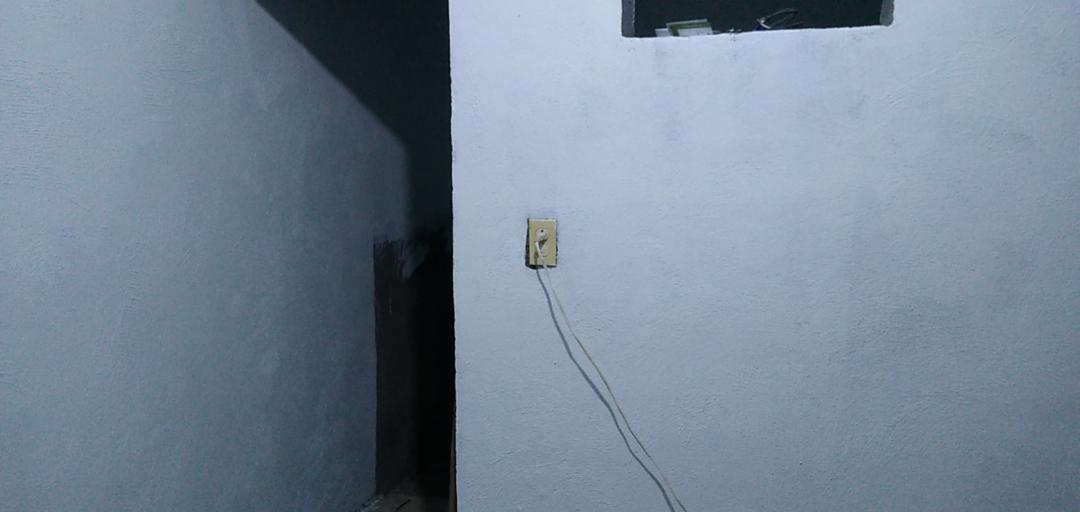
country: MX
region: Baja California
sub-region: Tijuana
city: Ejido Javier Rojo Gomez
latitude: 32.5504
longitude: -116.8820
